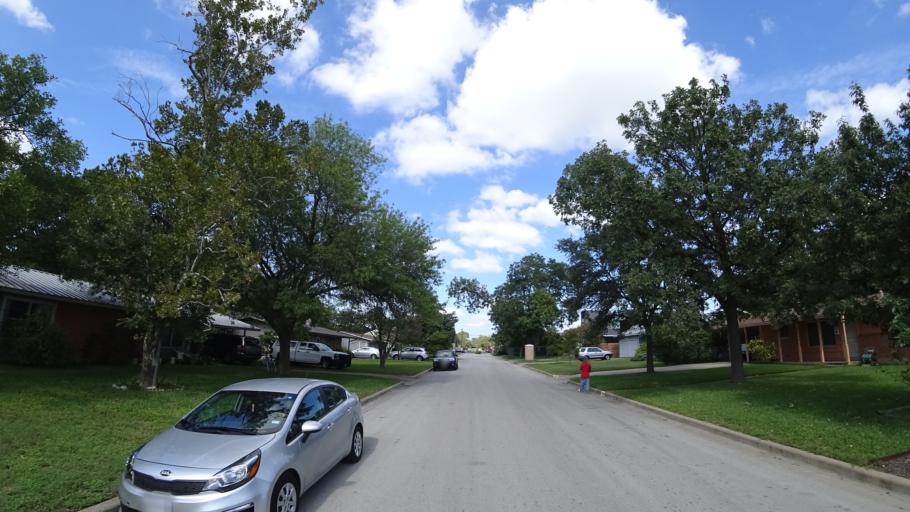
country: US
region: Texas
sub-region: Travis County
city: Austin
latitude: 30.3528
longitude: -97.7267
